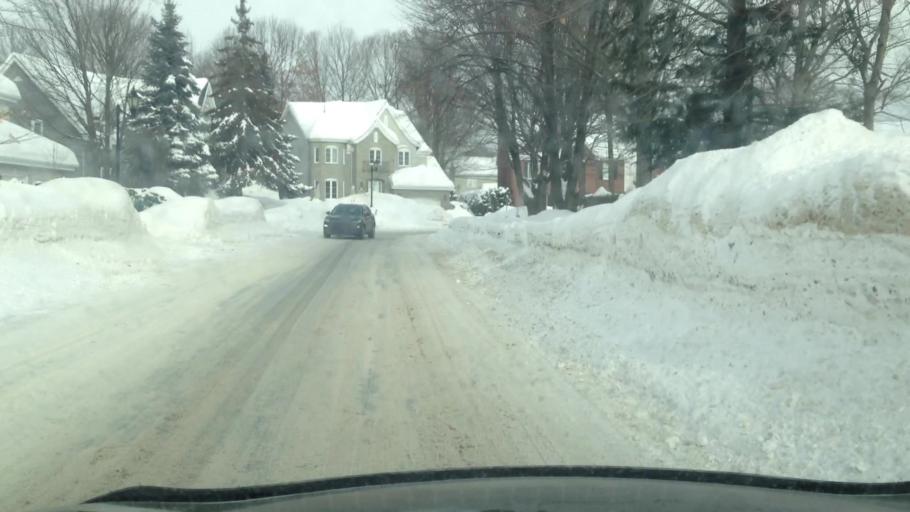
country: CA
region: Quebec
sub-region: Laurentides
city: Saint-Jerome
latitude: 45.7927
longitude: -74.0410
